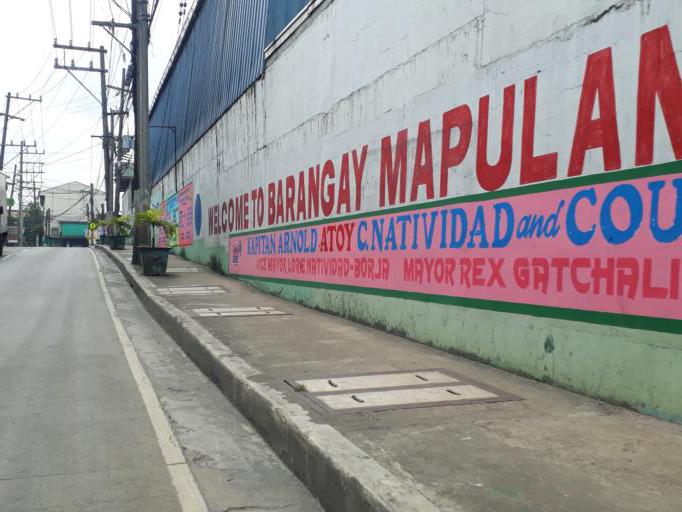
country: PH
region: Calabarzon
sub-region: Province of Rizal
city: Valenzuela
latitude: 14.7026
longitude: 120.9987
